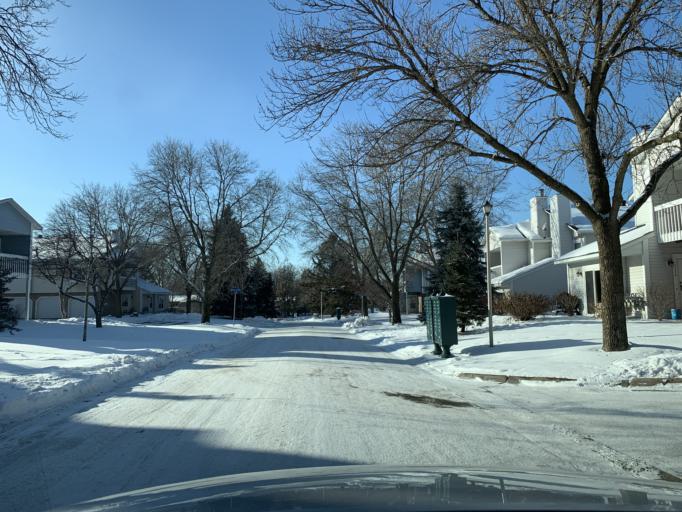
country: US
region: Minnesota
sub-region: Scott County
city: Savage
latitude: 44.8279
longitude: -93.3515
